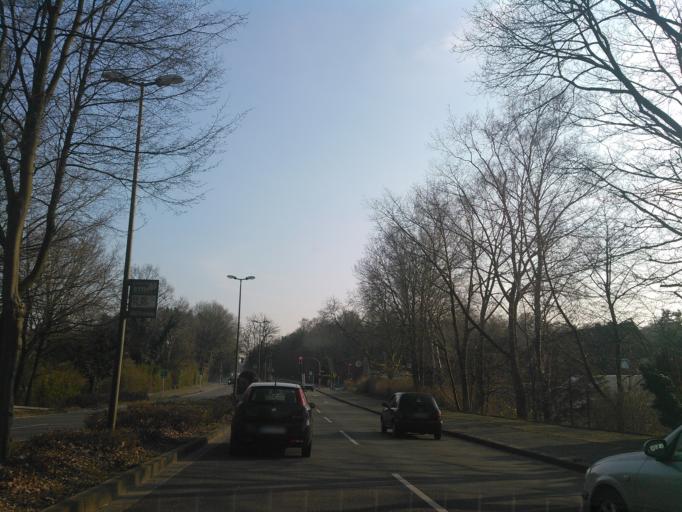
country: DE
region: North Rhine-Westphalia
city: Marl
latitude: 51.6737
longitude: 7.1017
